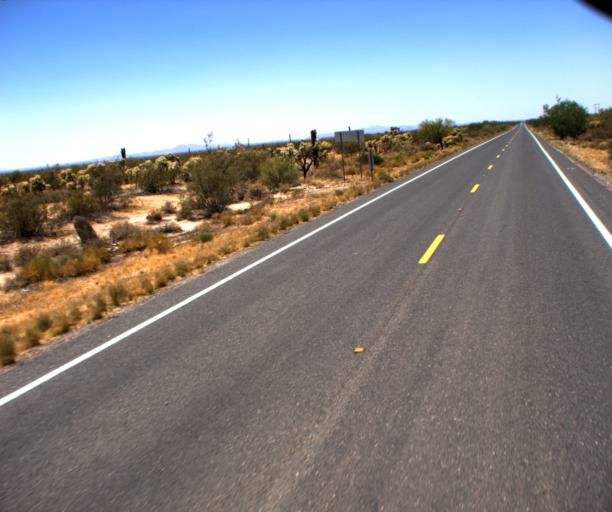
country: US
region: Arizona
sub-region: Pinal County
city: Florence
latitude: 32.8716
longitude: -111.2509
